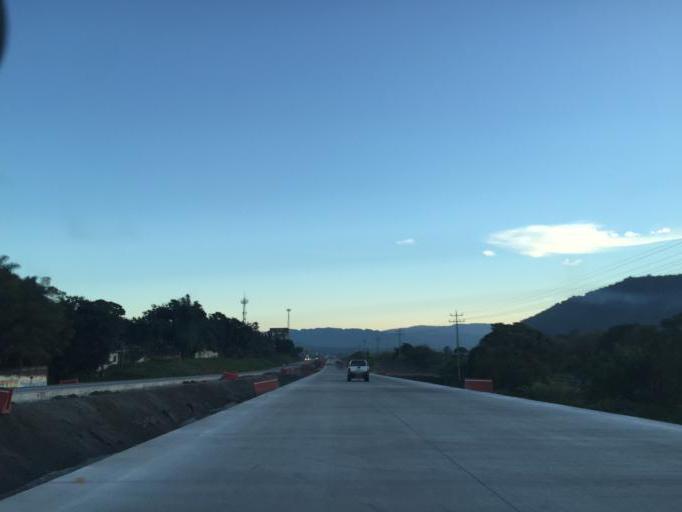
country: MX
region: Veracruz
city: Ixtac Zoquitlan
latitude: 18.8734
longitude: -97.0613
